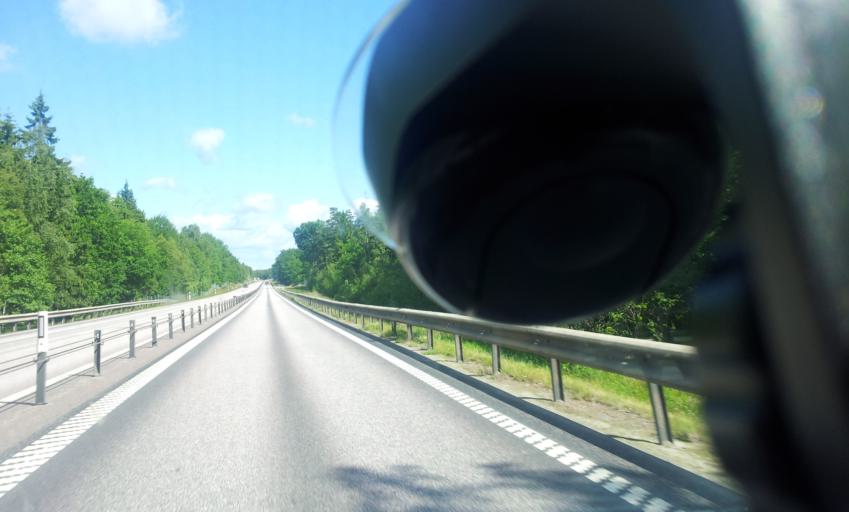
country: SE
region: Kalmar
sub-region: Oskarshamns Kommun
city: Paskallavik
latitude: 57.1682
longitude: 16.4439
